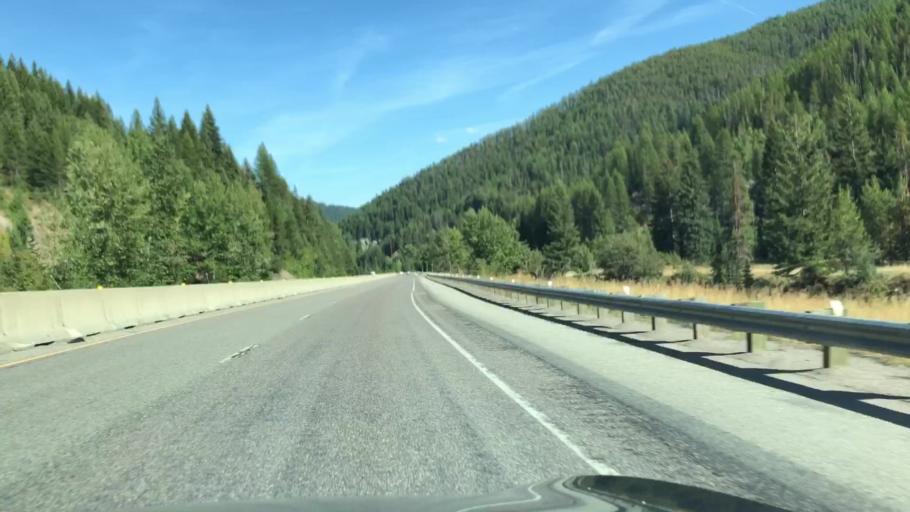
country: US
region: Montana
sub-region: Sanders County
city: Thompson Falls
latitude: 47.4178
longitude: -115.5553
